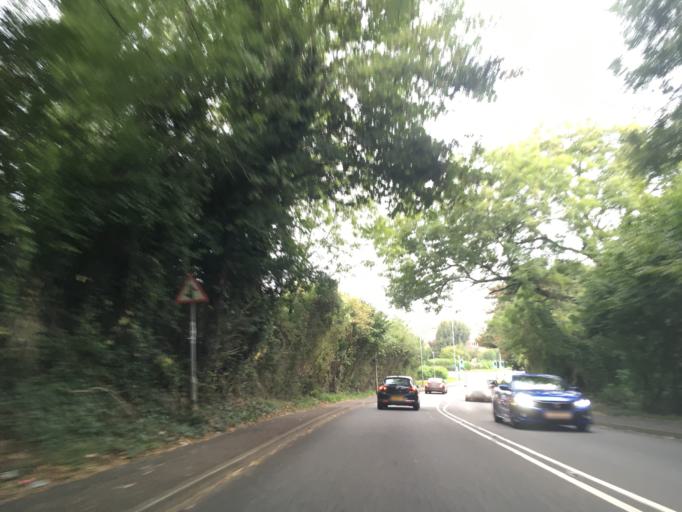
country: GB
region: Wales
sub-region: Monmouthshire
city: Chepstow
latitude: 51.6420
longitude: -2.6888
